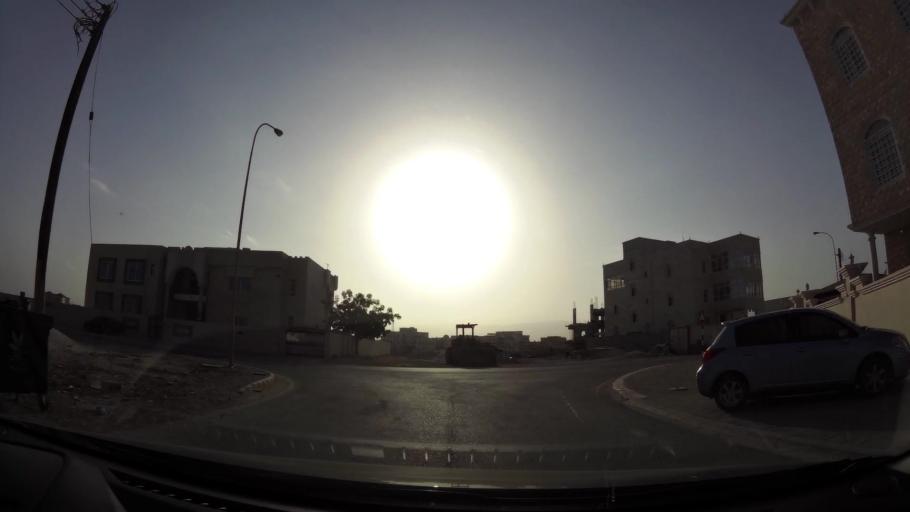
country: OM
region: Zufar
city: Salalah
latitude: 16.9998
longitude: 54.0278
